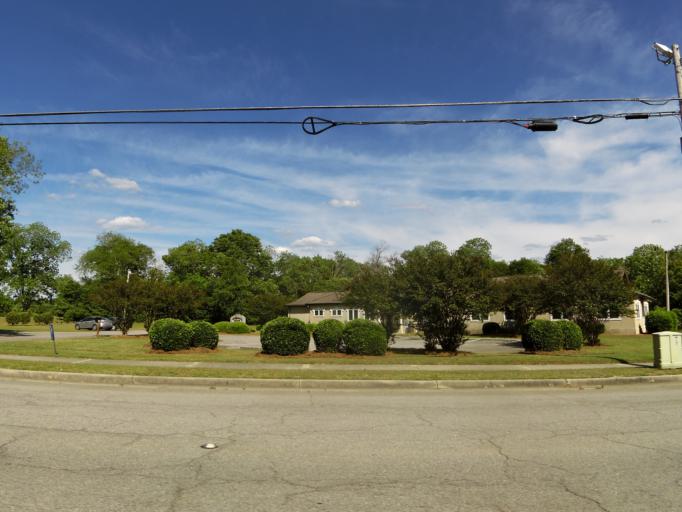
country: US
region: South Carolina
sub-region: Bamberg County
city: Denmark
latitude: 33.3138
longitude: -81.1437
